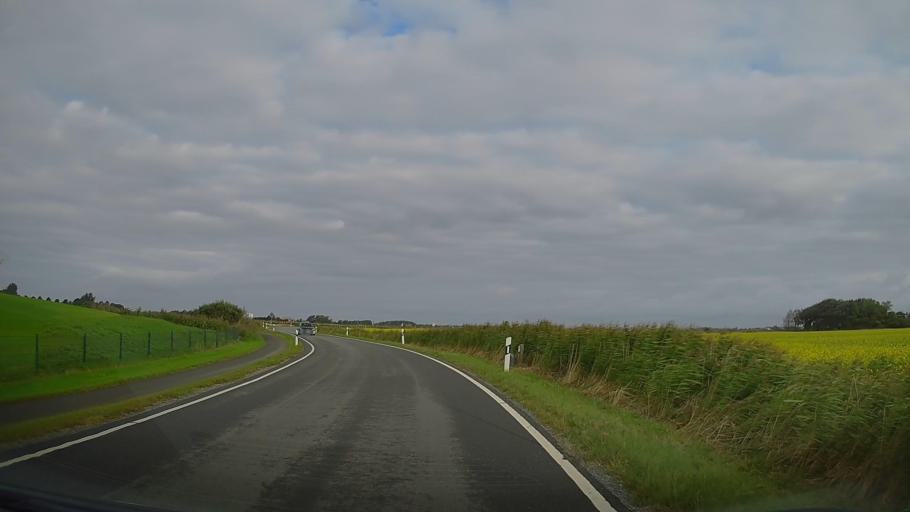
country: DE
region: Schleswig-Holstein
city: Ockholm
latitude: 54.6619
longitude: 8.8372
